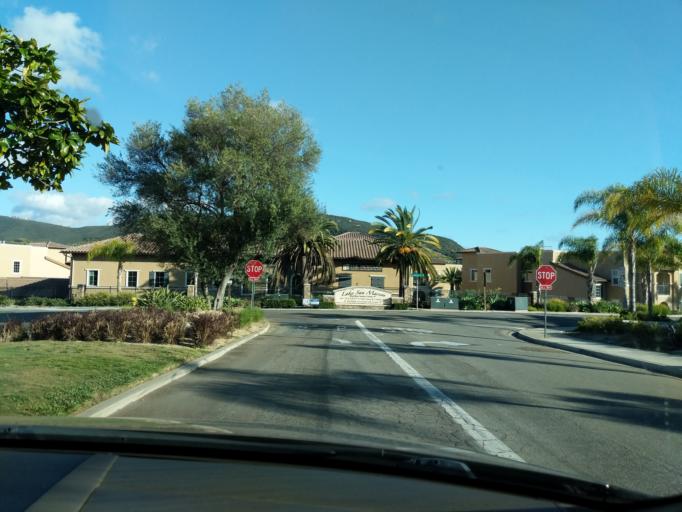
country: US
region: California
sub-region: San Diego County
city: Lake San Marcos
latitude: 33.1254
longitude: -117.2106
